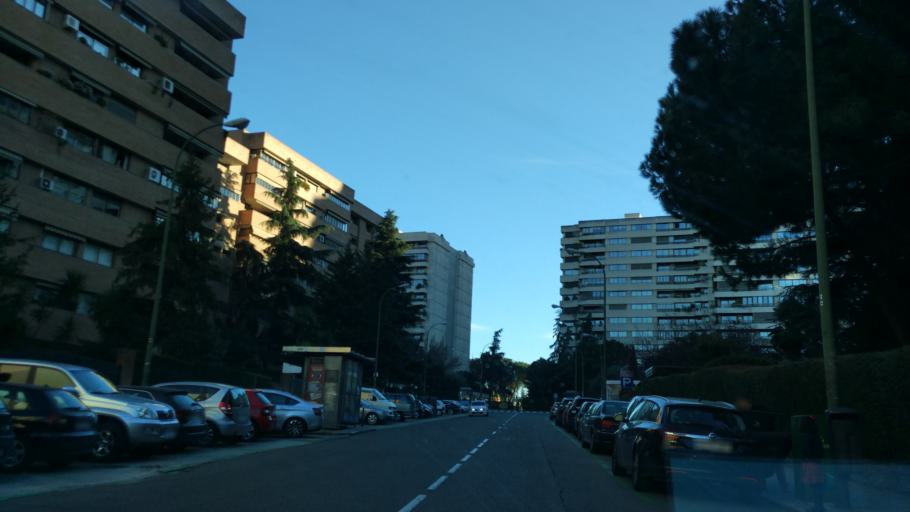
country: ES
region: Madrid
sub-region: Provincia de Madrid
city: Pinar de Chamartin
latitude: 40.4837
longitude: -3.6938
